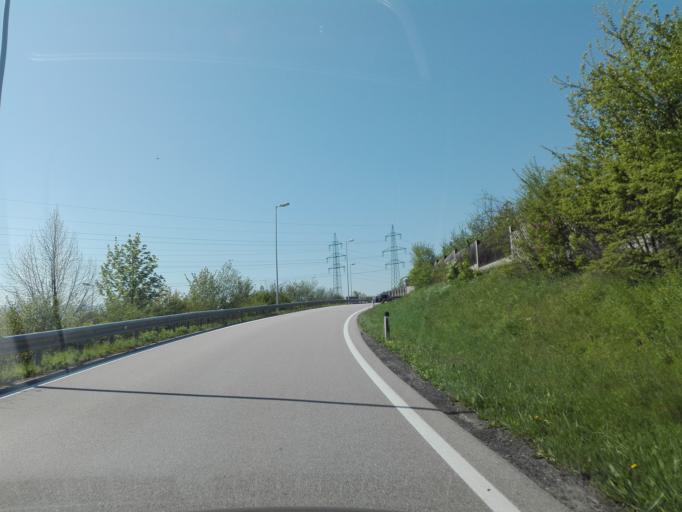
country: AT
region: Lower Austria
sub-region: Politischer Bezirk Amstetten
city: Haidershofen
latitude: 48.0711
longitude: 14.4279
